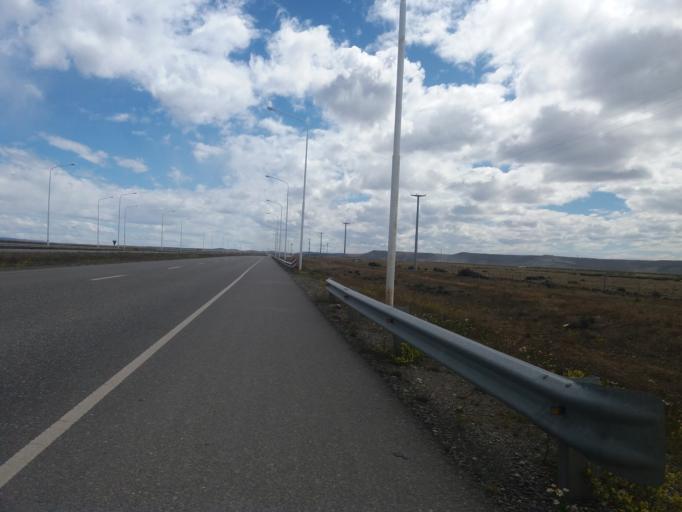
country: AR
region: Santa Cruz
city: Rio Gallegos
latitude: -51.6217
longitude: -69.4774
